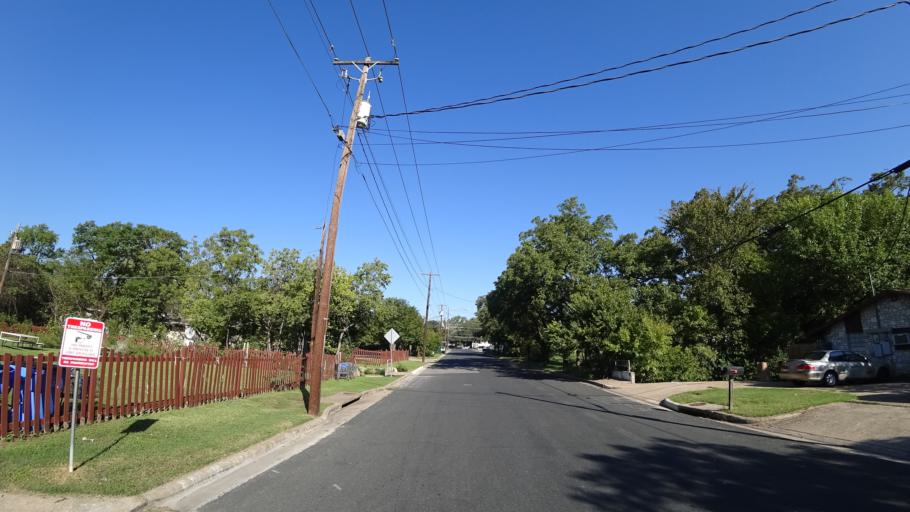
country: US
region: Texas
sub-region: Travis County
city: Wells Branch
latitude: 30.3551
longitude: -97.7001
